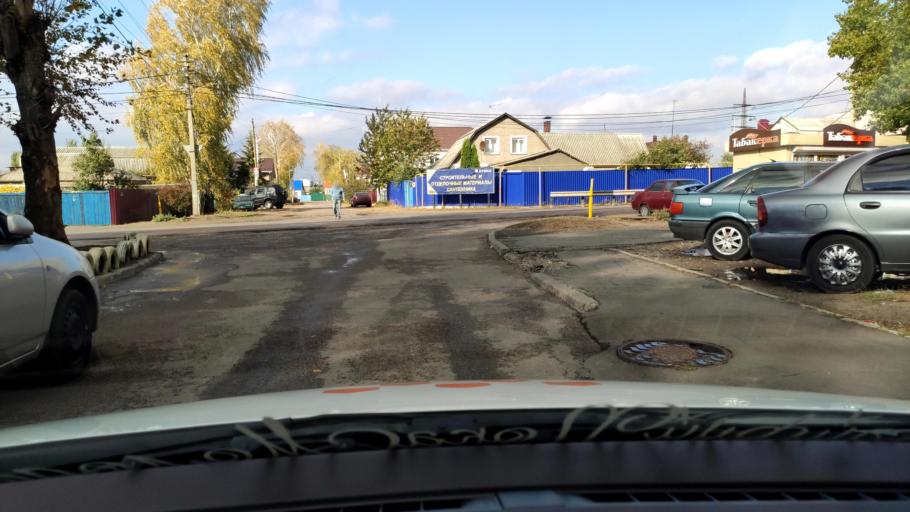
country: RU
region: Voronezj
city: Pridonskoy
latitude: 51.6871
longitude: 39.0800
